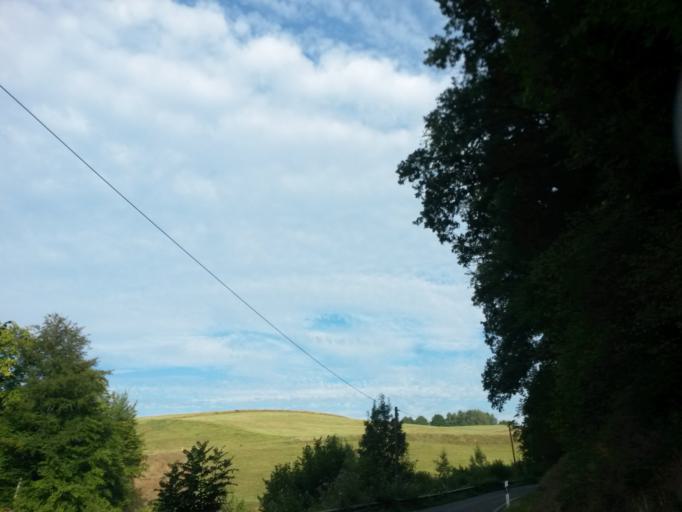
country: DE
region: North Rhine-Westphalia
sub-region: Regierungsbezirk Koln
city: Rosrath
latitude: 50.8862
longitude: 7.2196
